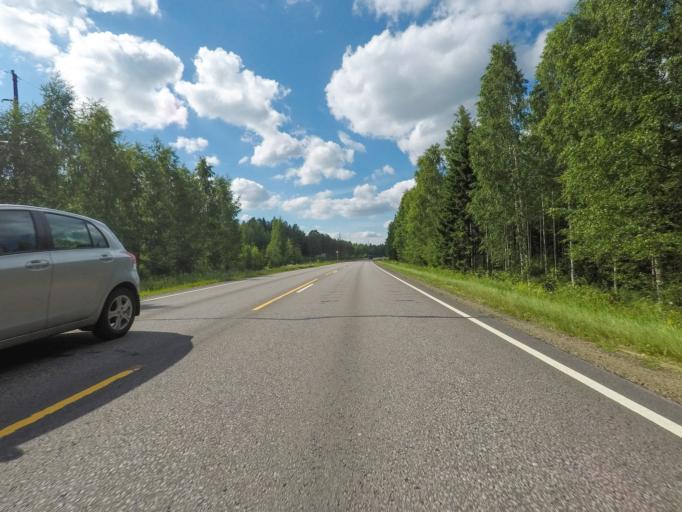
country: FI
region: Southern Savonia
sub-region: Savonlinna
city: Kerimaeki
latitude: 61.8464
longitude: 29.1846
